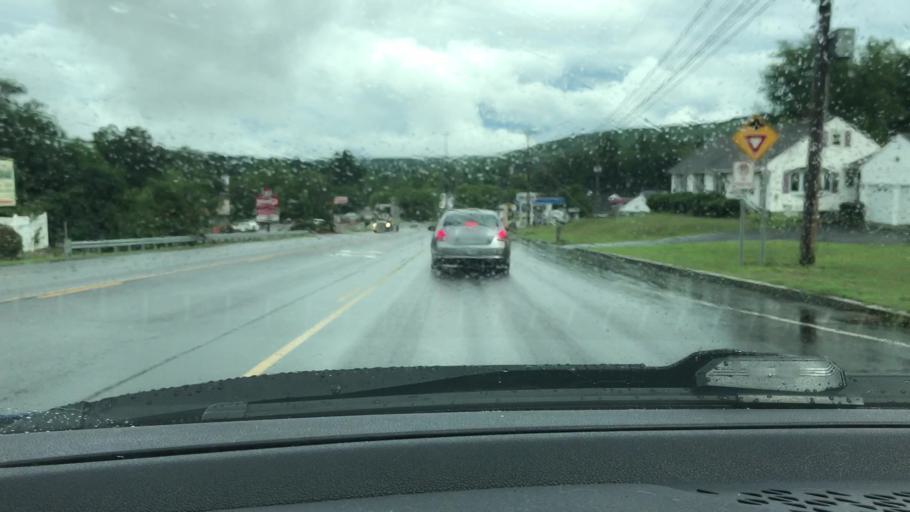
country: US
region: New Hampshire
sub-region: Merrimack County
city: Epsom
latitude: 43.2288
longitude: -71.3640
